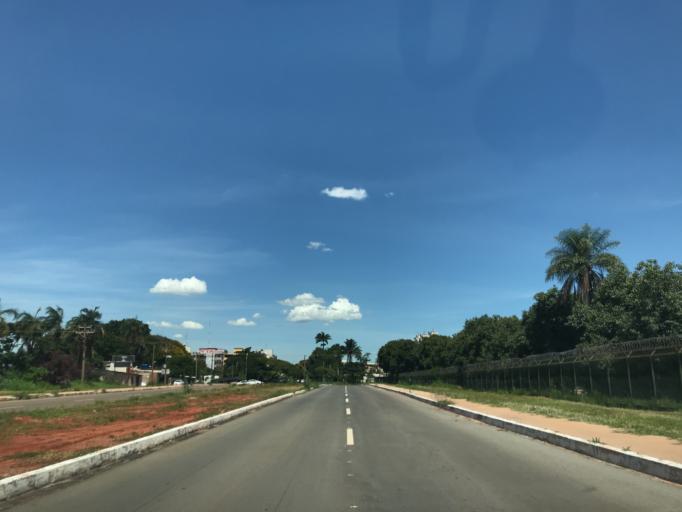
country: BR
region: Federal District
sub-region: Brasilia
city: Brasilia
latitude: -15.7759
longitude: -47.8935
